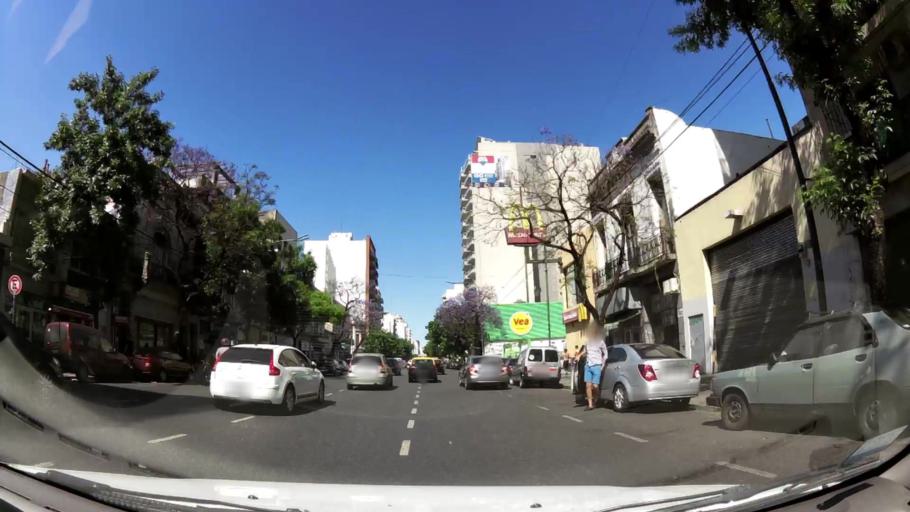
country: AR
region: Buenos Aires F.D.
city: Buenos Aires
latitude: -34.6241
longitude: -58.4052
